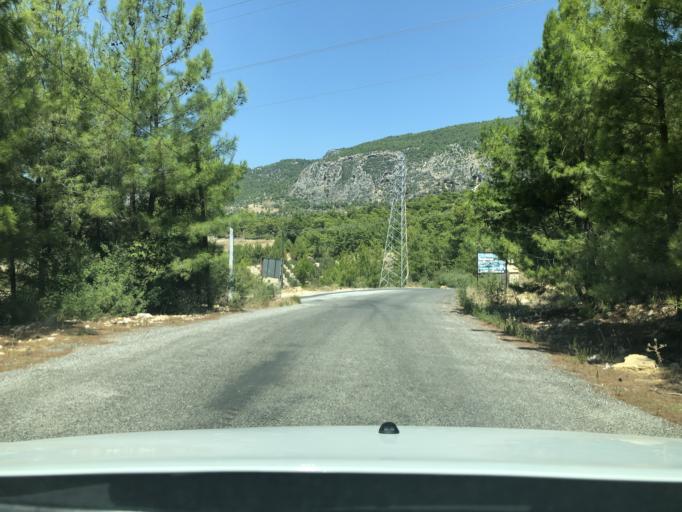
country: TR
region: Antalya
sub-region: Manavgat
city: Manavgat
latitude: 36.8757
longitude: 31.5498
